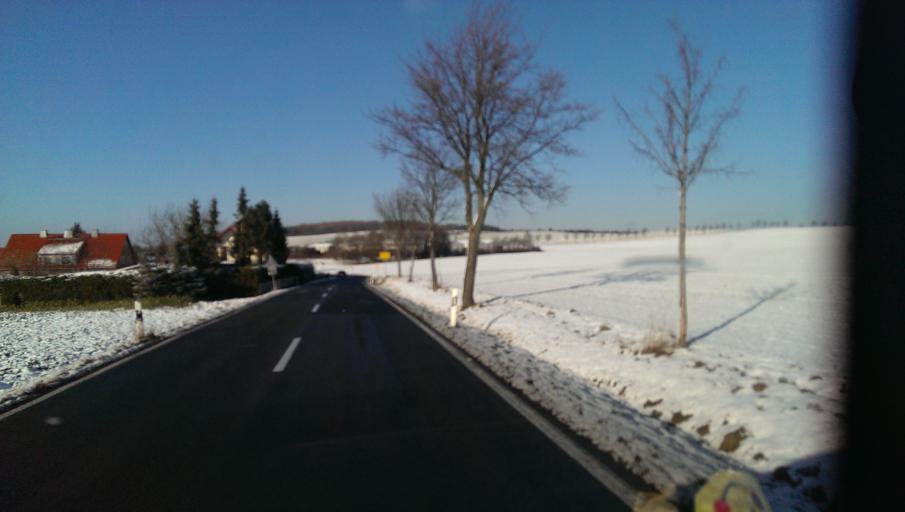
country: DE
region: Saxony
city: Obercunnersdorf
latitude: 50.9046
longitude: 13.6098
